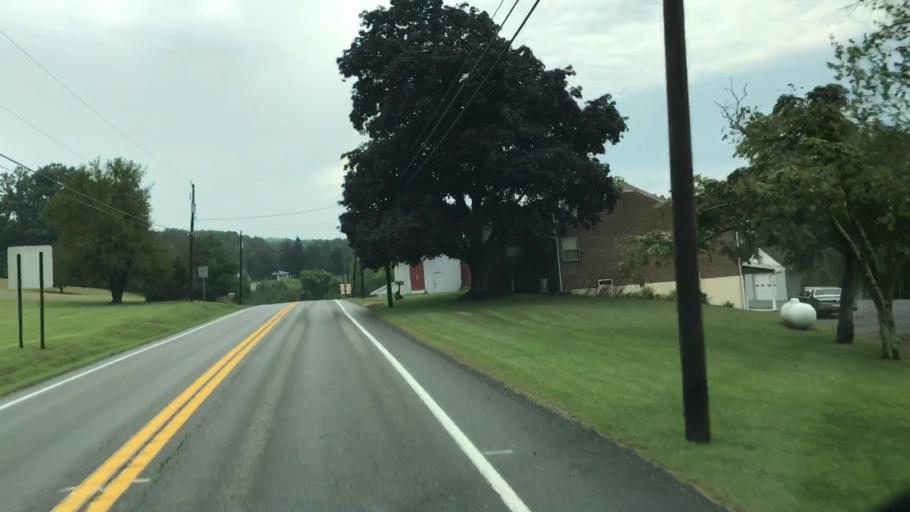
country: US
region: Pennsylvania
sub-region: Perry County
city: New Bloomfield
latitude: 40.3844
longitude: -77.1440
